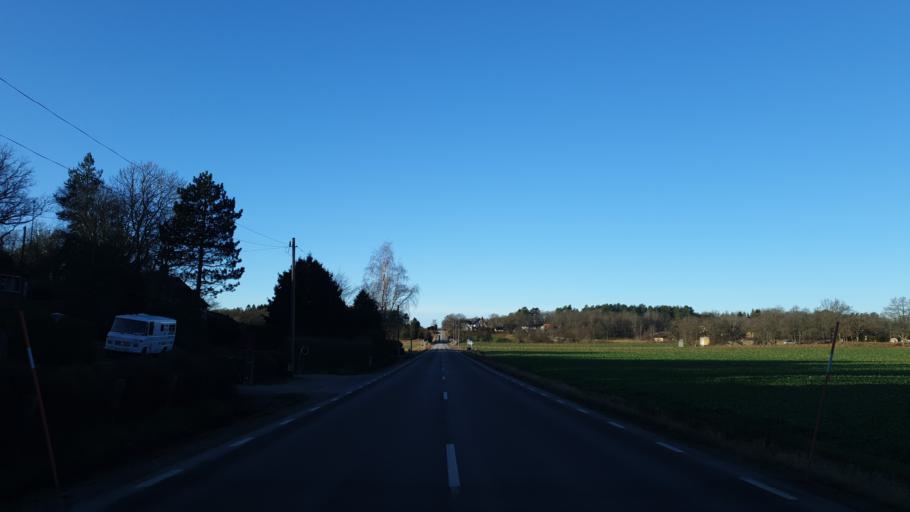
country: SE
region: Blekinge
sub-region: Ronneby Kommun
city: Ronneby
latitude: 56.1945
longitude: 15.3430
